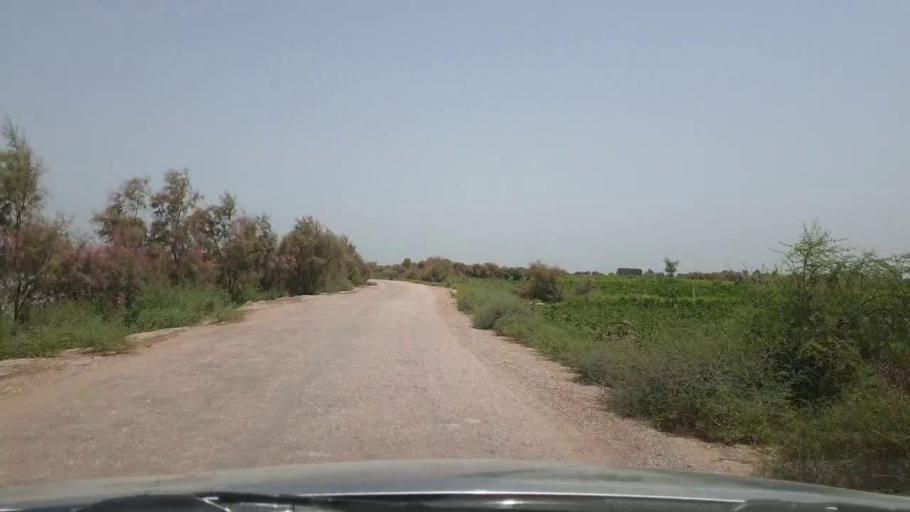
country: PK
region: Sindh
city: Pano Aqil
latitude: 27.8709
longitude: 69.1605
